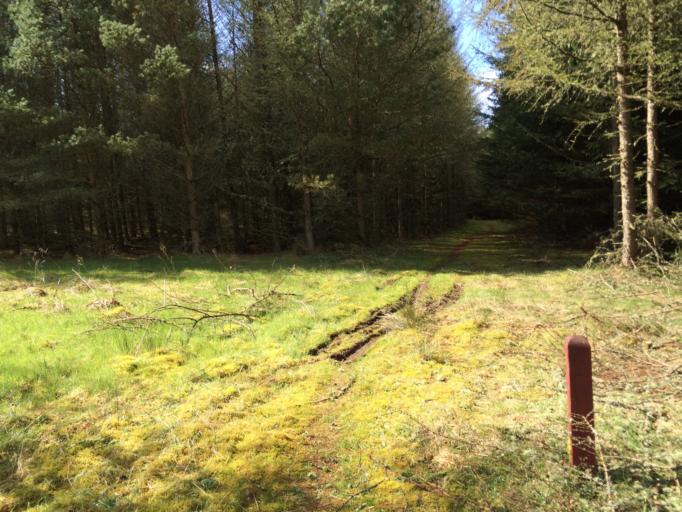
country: DK
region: Central Jutland
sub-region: Holstebro Kommune
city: Ulfborg
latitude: 56.2383
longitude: 8.3976
